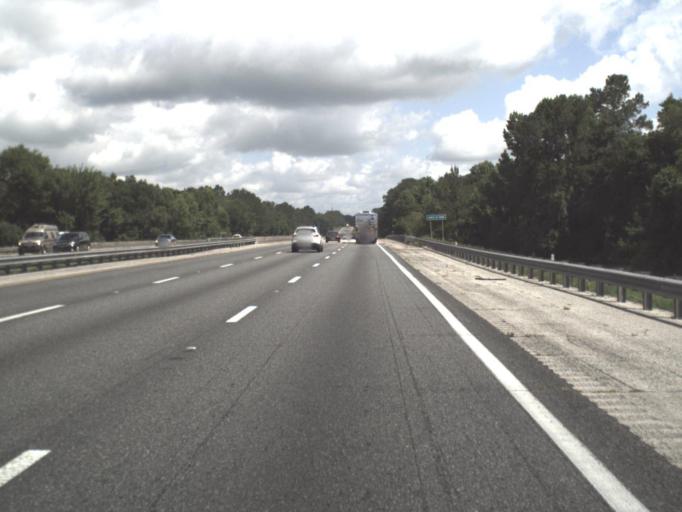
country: US
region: Florida
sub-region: Alachua County
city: High Springs
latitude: 29.9253
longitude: -82.5580
